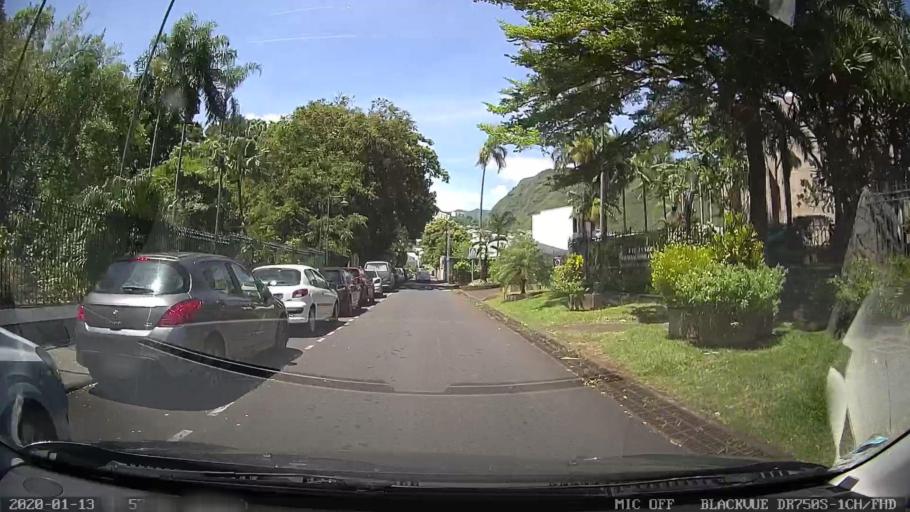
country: RE
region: Reunion
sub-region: Reunion
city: Saint-Denis
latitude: -20.8867
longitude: 55.4501
